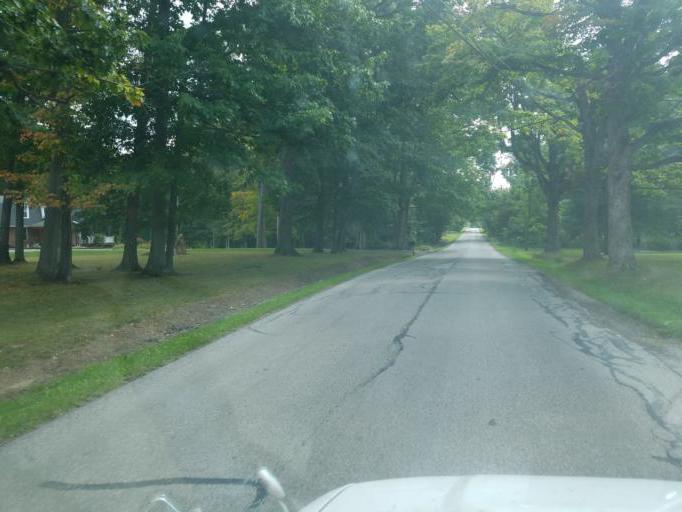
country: US
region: Ohio
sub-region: Geauga County
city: Middlefield
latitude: 41.4561
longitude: -81.1087
